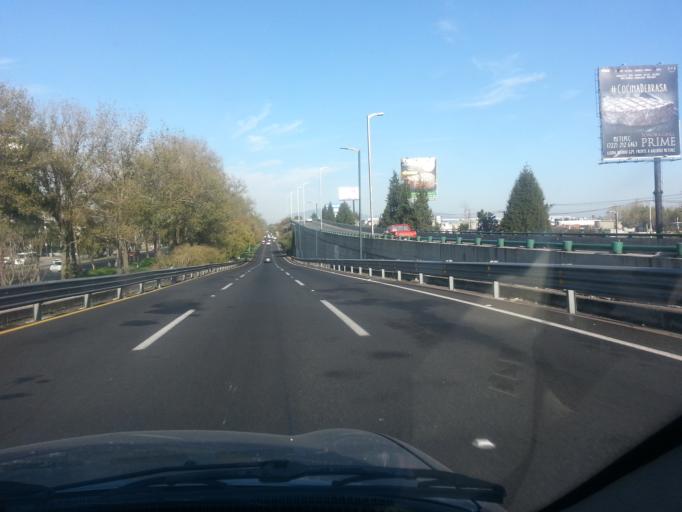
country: MX
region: Mexico
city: Santa Maria Totoltepec
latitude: 19.2869
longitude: -99.5741
